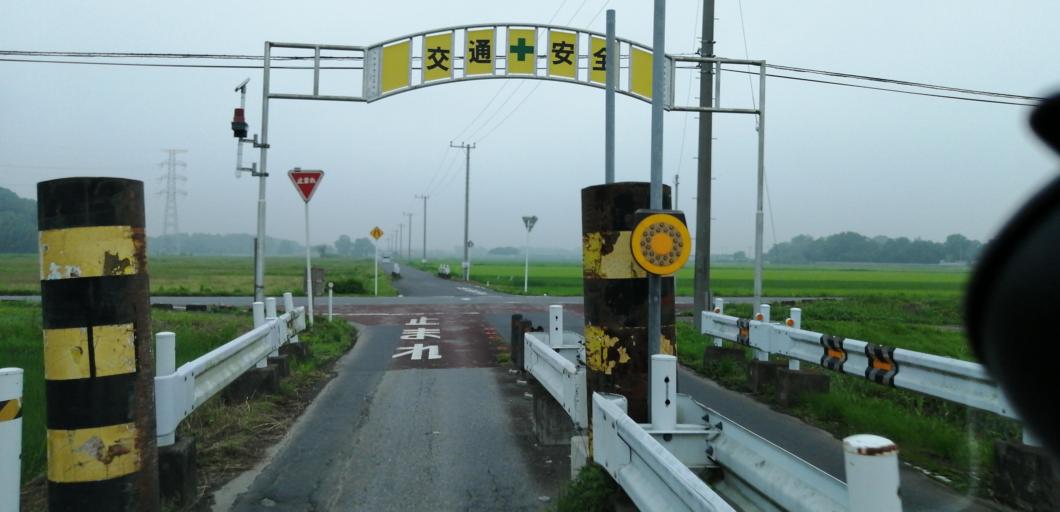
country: JP
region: Chiba
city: Noda
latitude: 35.9948
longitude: 139.8671
